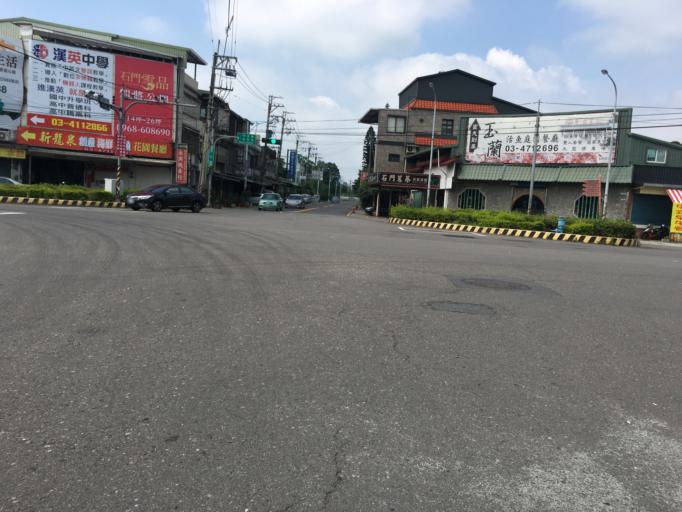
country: TW
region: Taiwan
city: Daxi
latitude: 24.8488
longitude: 121.2447
